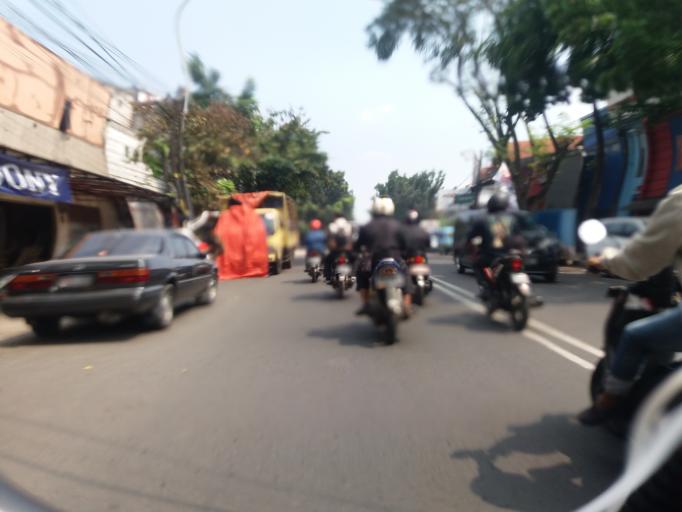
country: ID
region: West Java
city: Bandung
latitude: -6.9074
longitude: 107.5845
